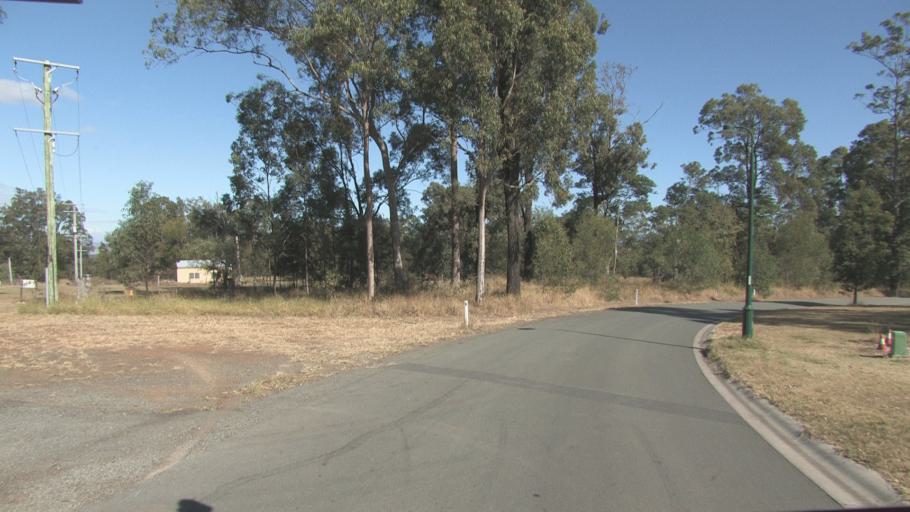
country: AU
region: Queensland
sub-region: Logan
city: Cedar Vale
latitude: -27.8954
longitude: 153.0014
